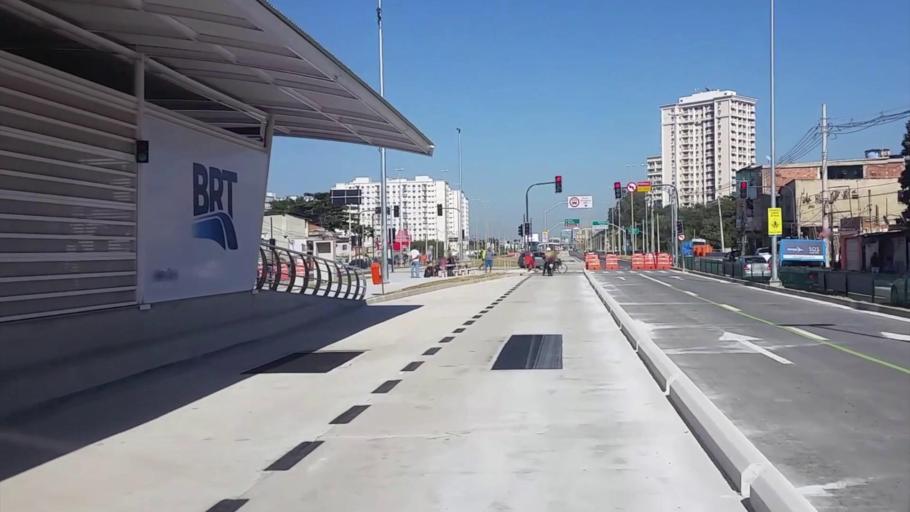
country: BR
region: Rio de Janeiro
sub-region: Nilopolis
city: Nilopolis
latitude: -22.9635
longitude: -43.3941
